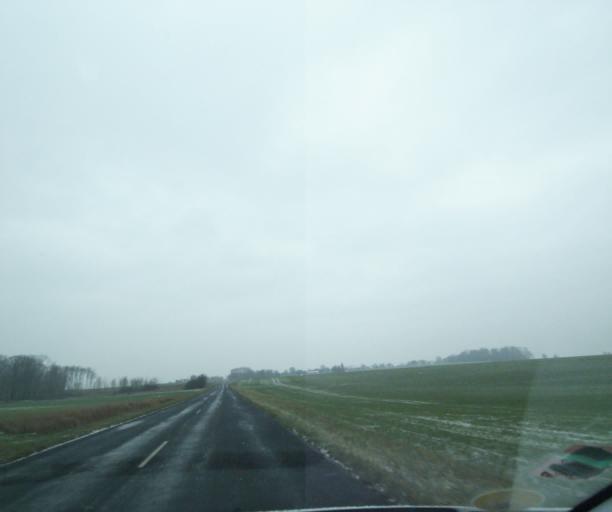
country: FR
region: Champagne-Ardenne
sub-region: Departement de la Haute-Marne
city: Wassy
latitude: 48.4677
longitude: 5.0265
